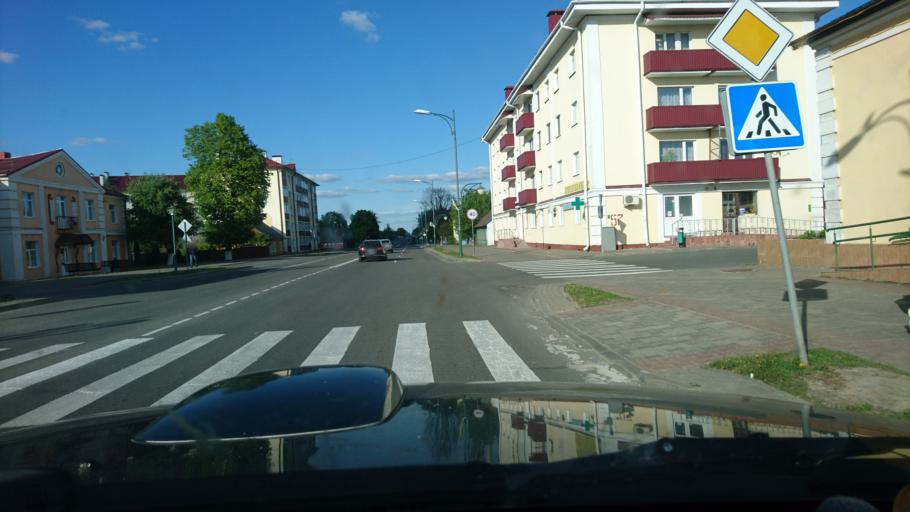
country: BY
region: Brest
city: Byaroza
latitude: 52.5347
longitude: 24.9854
